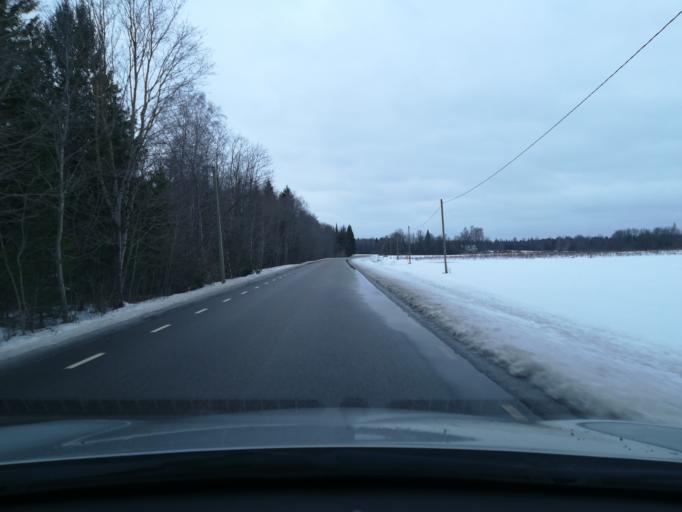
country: EE
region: Harju
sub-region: Nissi vald
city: Riisipere
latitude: 59.1293
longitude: 24.3026
